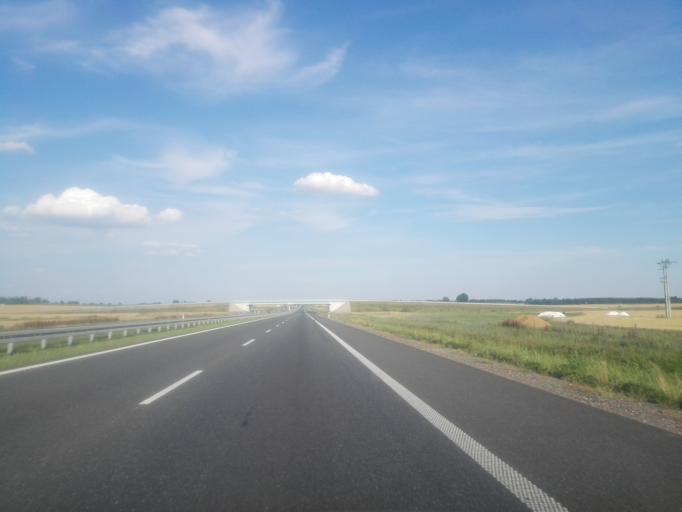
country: PL
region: Lower Silesian Voivodeship
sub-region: Powiat olesnicki
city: Sycow
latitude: 51.3038
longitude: 17.6287
